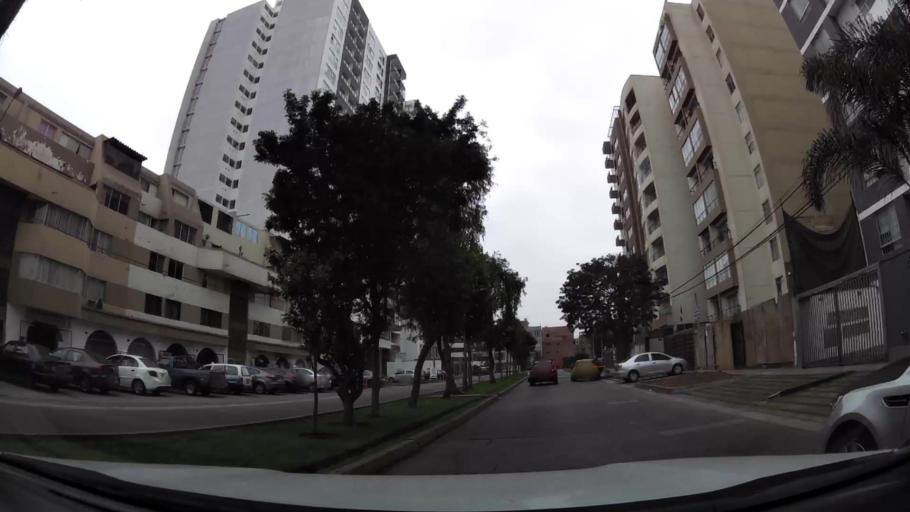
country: PE
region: Lima
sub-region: Lima
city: Surco
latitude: -12.1171
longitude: -77.0136
